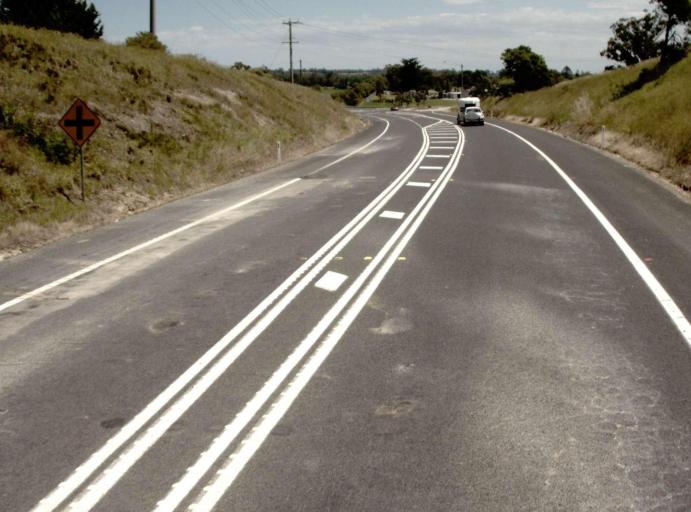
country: AU
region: Victoria
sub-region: East Gippsland
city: Lakes Entrance
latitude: -37.7054
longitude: 148.4707
